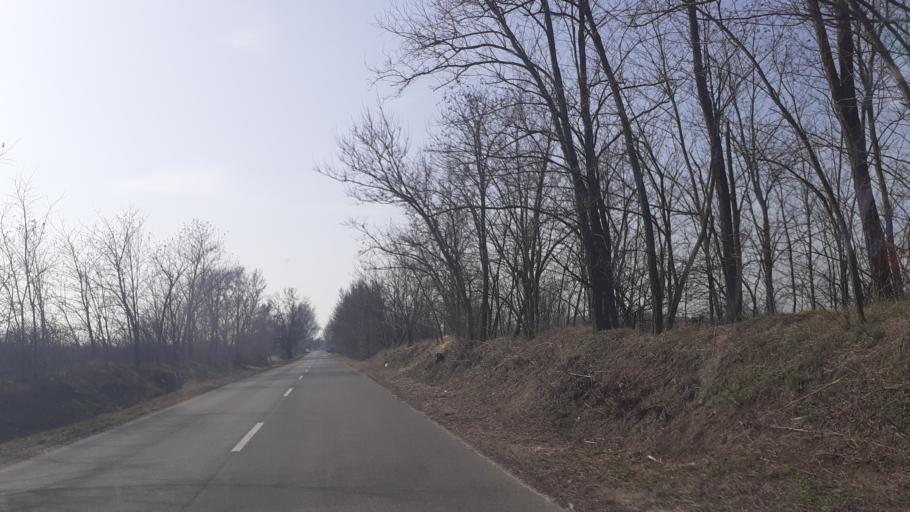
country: HU
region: Pest
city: Orkeny
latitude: 47.0889
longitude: 19.3793
